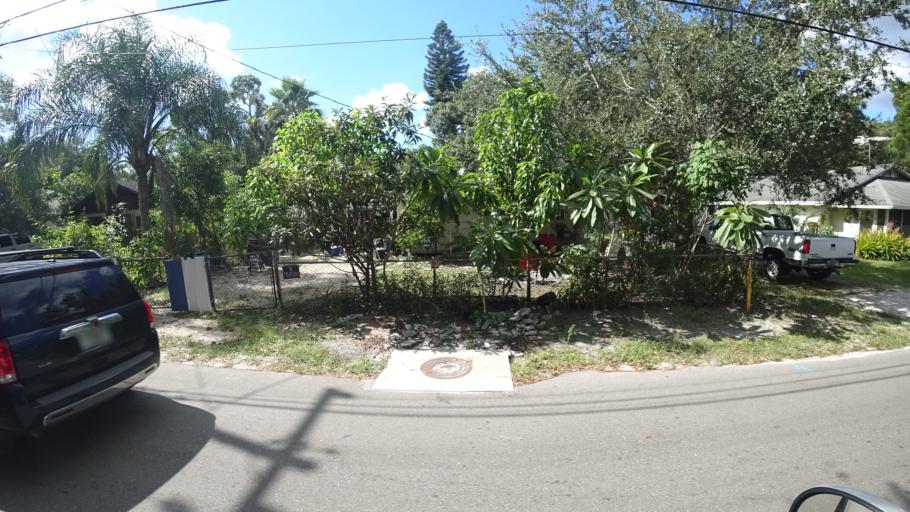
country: US
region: Florida
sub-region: Manatee County
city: West Samoset
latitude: 27.4744
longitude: -82.5688
